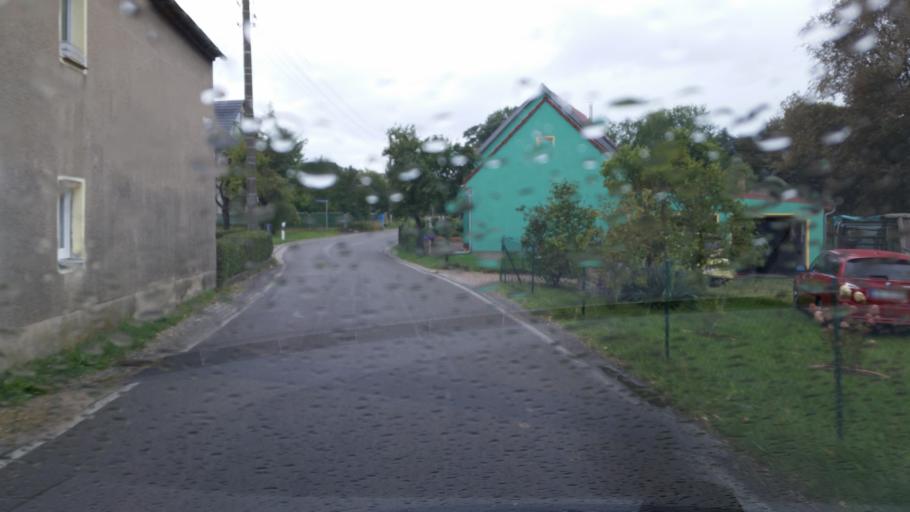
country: DE
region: Saxony
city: Haselbachtal
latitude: 51.2854
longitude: 14.0418
